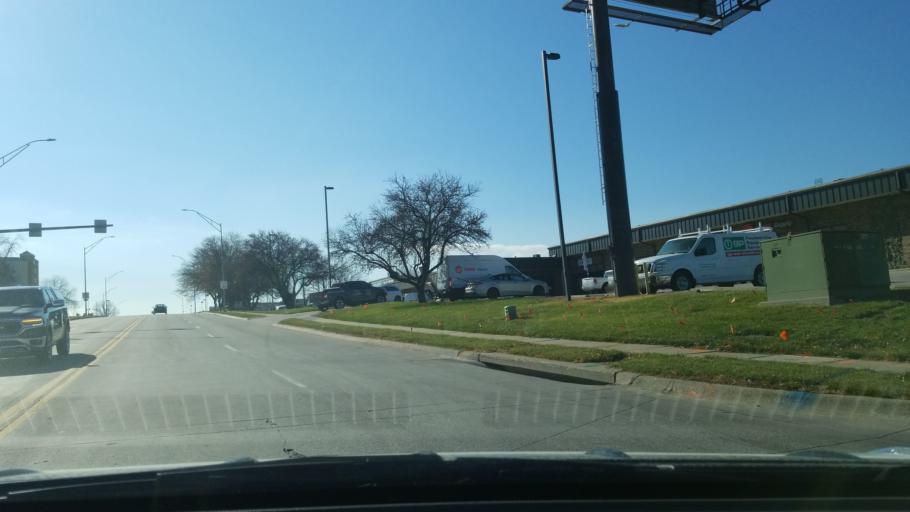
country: US
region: Nebraska
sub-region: Douglas County
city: Ralston
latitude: 41.2160
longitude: -96.0816
